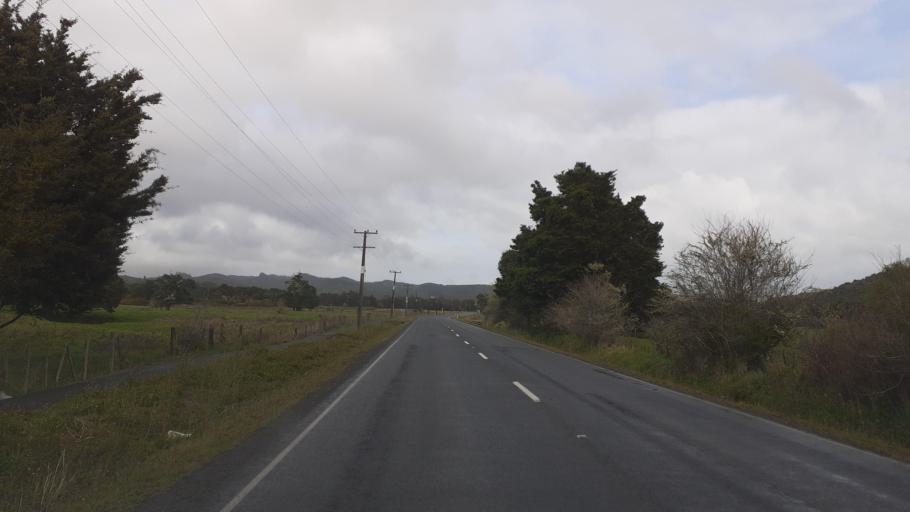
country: NZ
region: Northland
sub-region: Far North District
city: Moerewa
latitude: -35.3990
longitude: 173.9936
